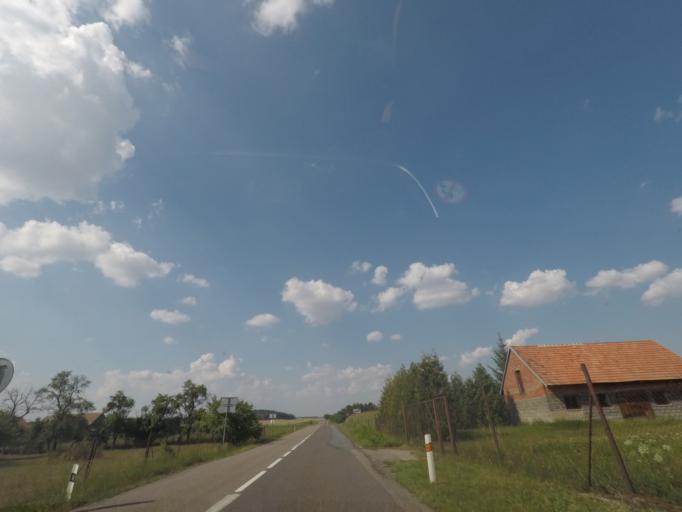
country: CZ
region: Kralovehradecky
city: Dolni Cernilov
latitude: 50.2422
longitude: 15.9646
